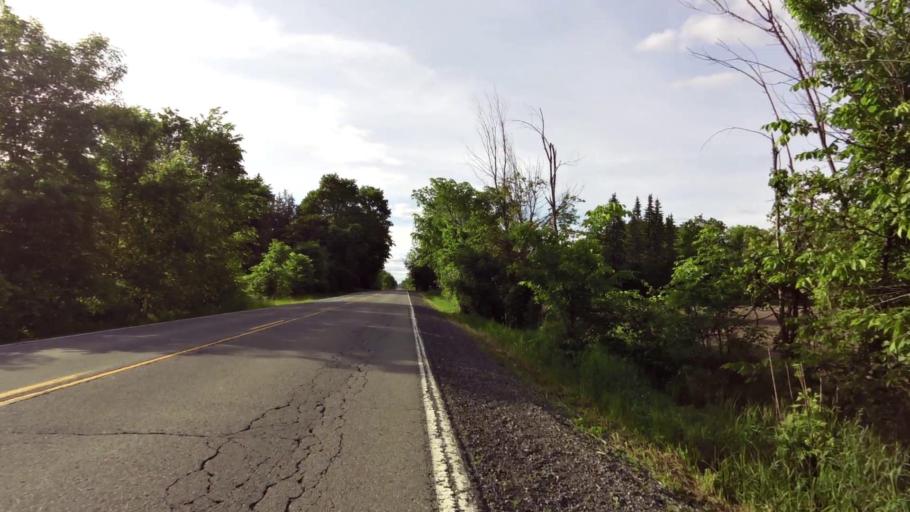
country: CA
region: Ontario
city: Ottawa
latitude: 45.2130
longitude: -75.5986
